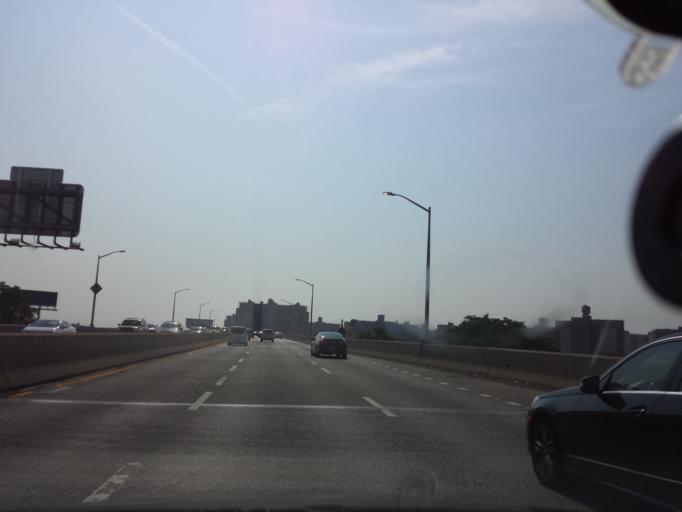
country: US
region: New York
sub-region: Kings County
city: Coney Island
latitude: 40.5834
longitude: -73.9837
